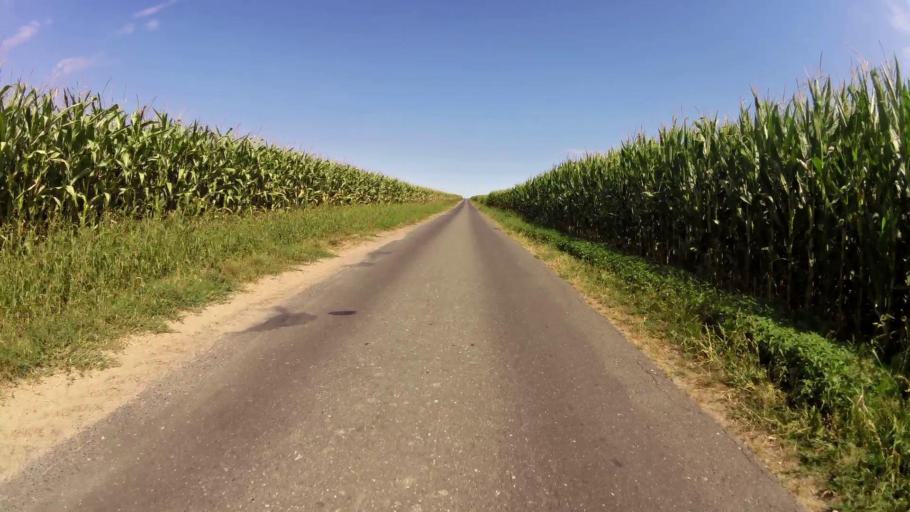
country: PL
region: West Pomeranian Voivodeship
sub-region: Powiat choszczenski
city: Choszczno
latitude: 53.2589
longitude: 15.4320
